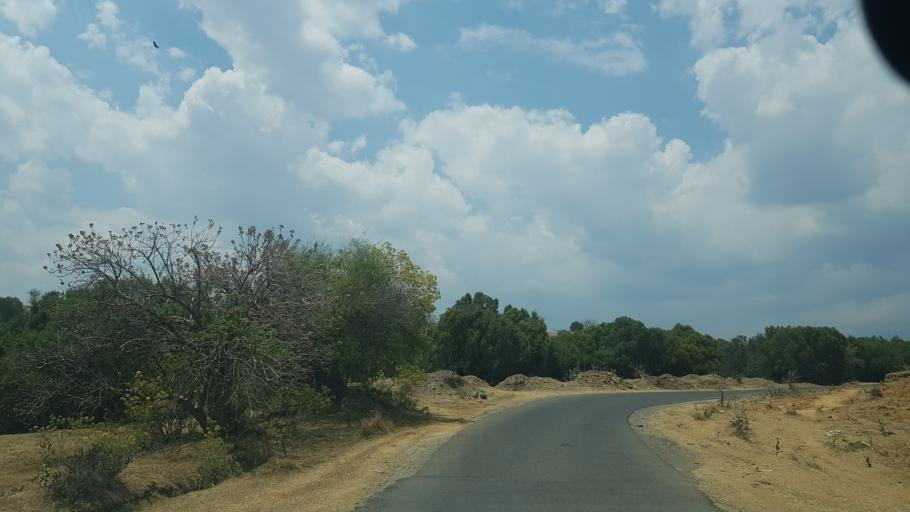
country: MX
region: Puebla
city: San Juan Amecac
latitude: 18.8143
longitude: -98.6246
